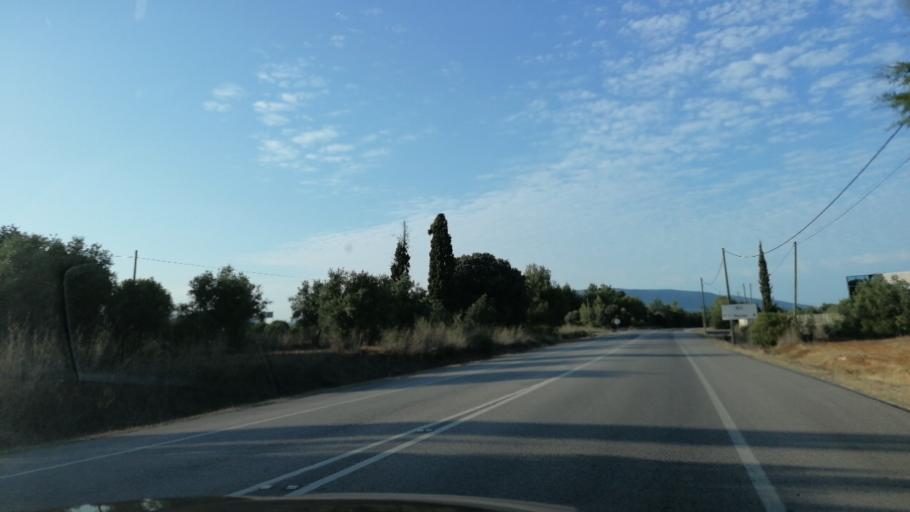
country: PT
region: Santarem
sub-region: Alcanena
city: Alcanena
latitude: 39.4372
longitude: -8.6257
